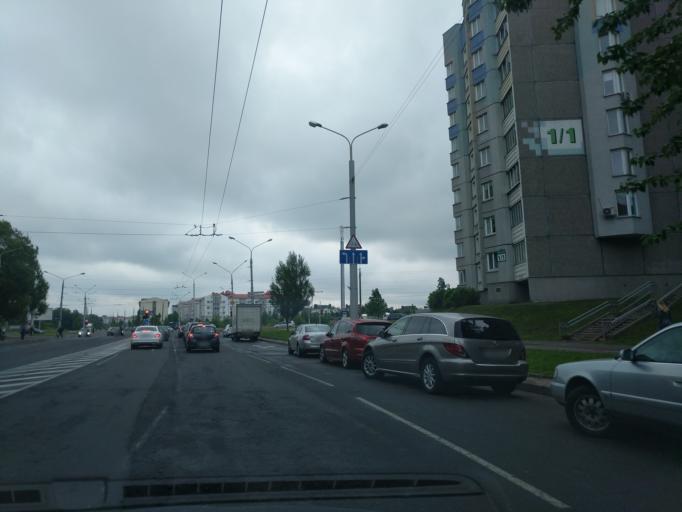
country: BY
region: Minsk
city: Novoye Medvezhino
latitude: 53.8991
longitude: 27.4609
